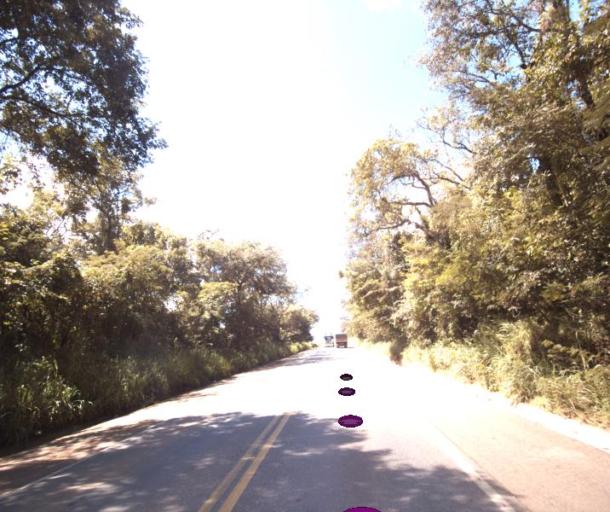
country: BR
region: Goias
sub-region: Pirenopolis
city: Pirenopolis
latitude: -16.0287
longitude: -49.0956
